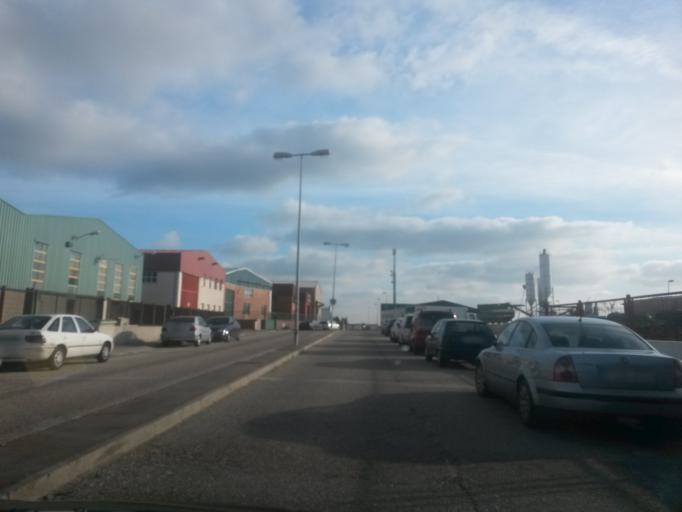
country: ES
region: Castille and Leon
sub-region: Provincia de Salamanca
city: San Cristobal de la Cuesta
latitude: 41.0082
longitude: -5.6124
